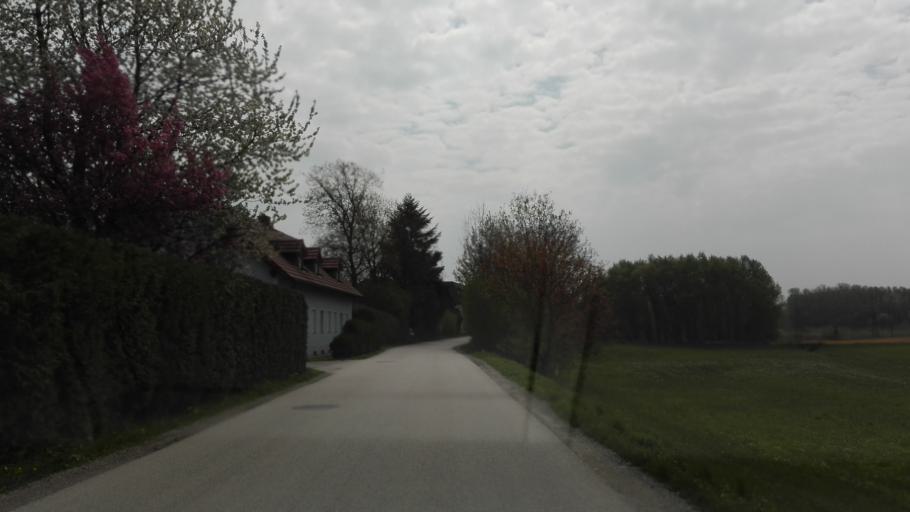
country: AT
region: Upper Austria
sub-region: Politischer Bezirk Perg
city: Perg
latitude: 48.2397
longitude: 14.5987
